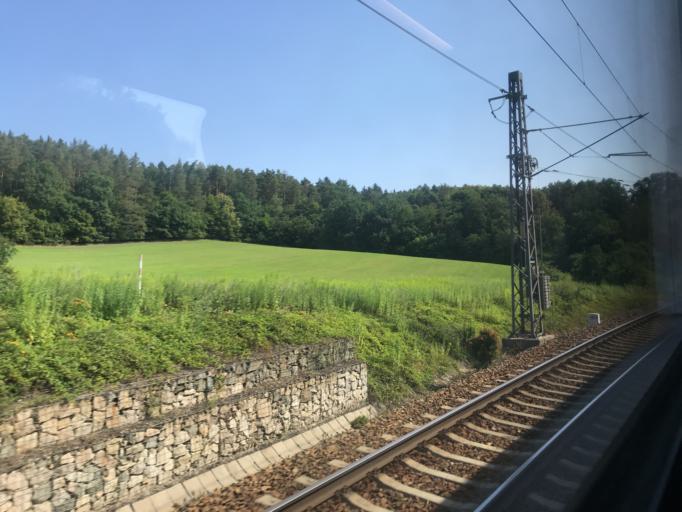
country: CZ
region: Central Bohemia
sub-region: Okres Benesov
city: Cercany
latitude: 49.8754
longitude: 14.7189
